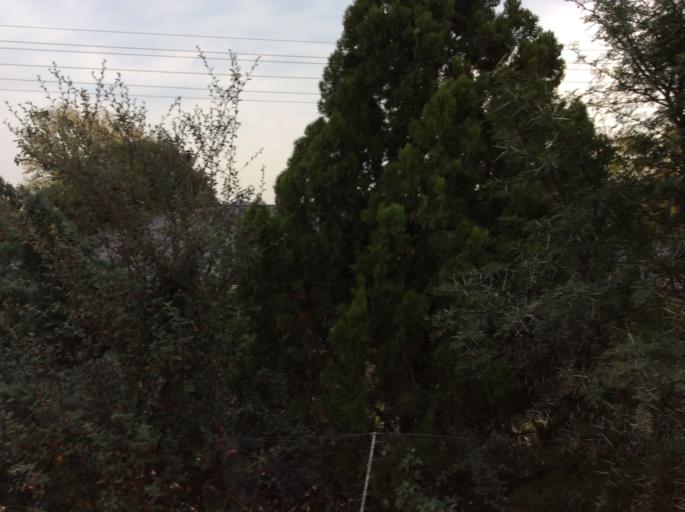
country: LS
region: Mafeteng
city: Mafeteng
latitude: -29.9888
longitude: 27.0108
